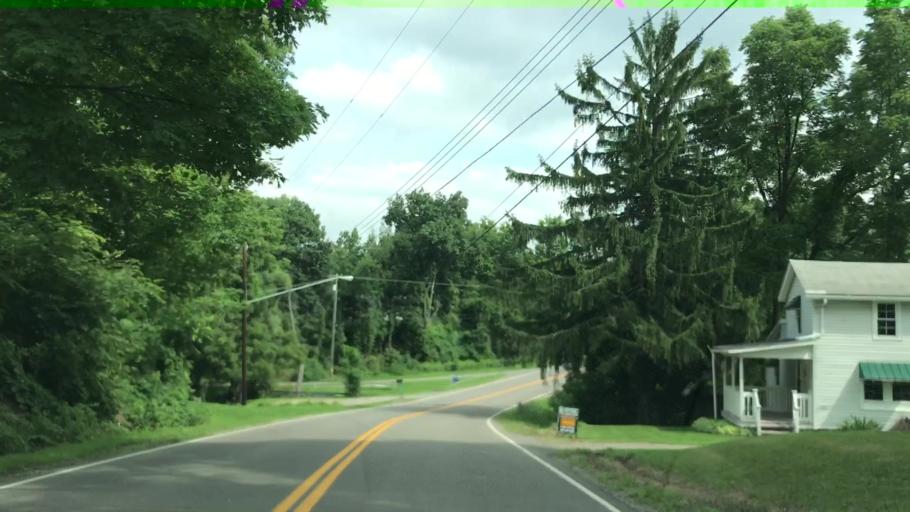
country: US
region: New York
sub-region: Steuben County
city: Sylvan Beach
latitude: 42.5230
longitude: -77.1689
